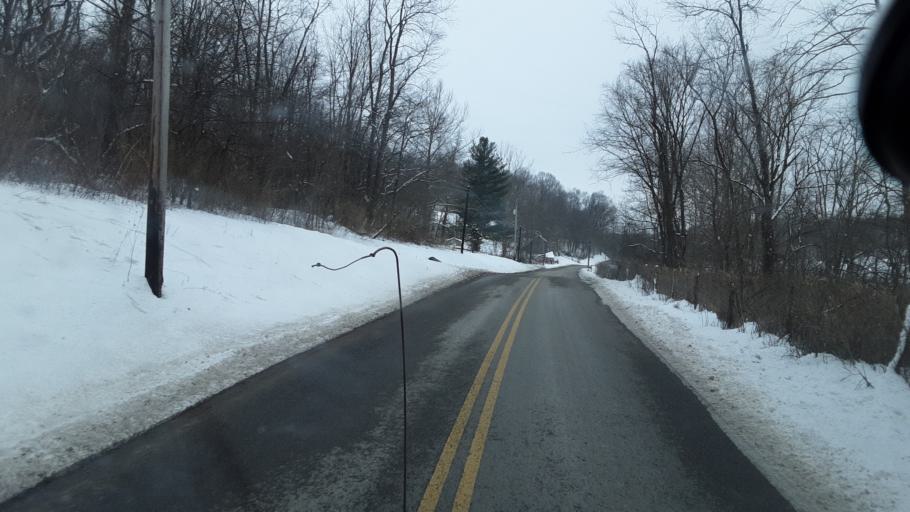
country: US
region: Ohio
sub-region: Perry County
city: Somerset
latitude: 39.9023
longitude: -82.2276
